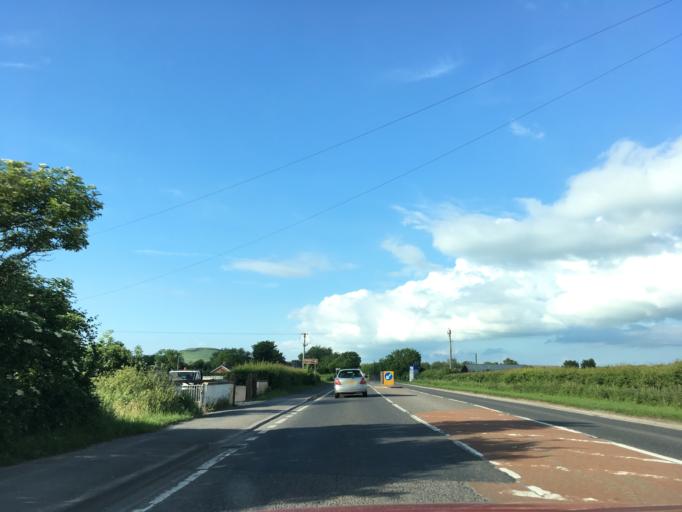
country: GB
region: England
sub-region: Somerset
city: Highbridge
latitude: 51.2296
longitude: -2.9611
